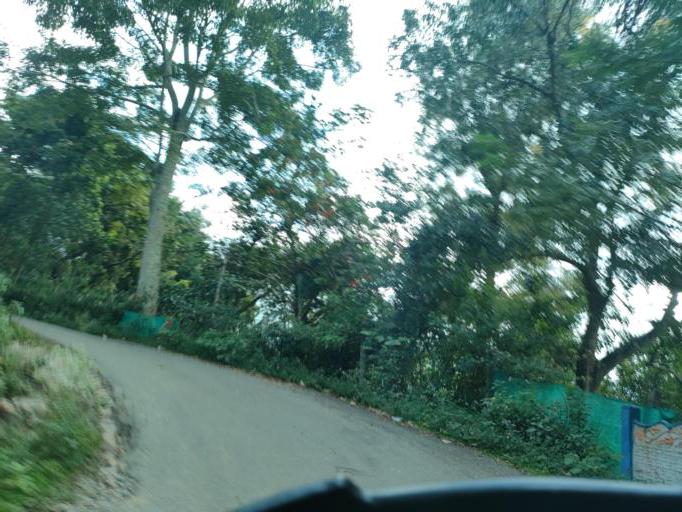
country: IN
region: Tamil Nadu
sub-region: Dindigul
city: Kodaikanal
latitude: 10.2748
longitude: 77.5336
